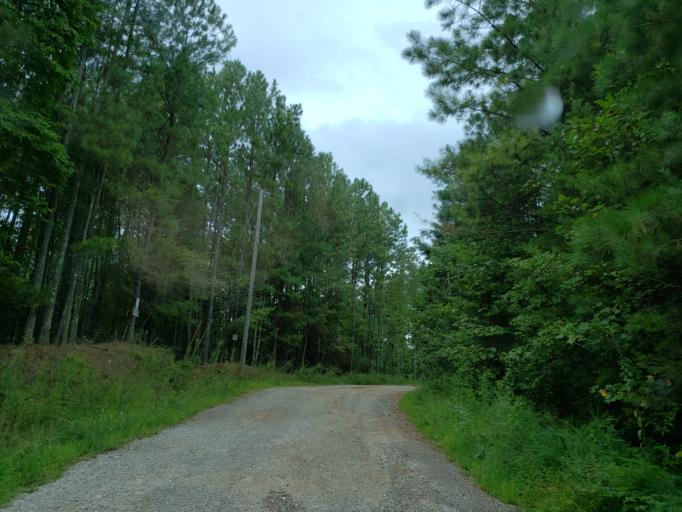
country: US
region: Georgia
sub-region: Gilmer County
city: Ellijay
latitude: 34.5699
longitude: -84.5238
